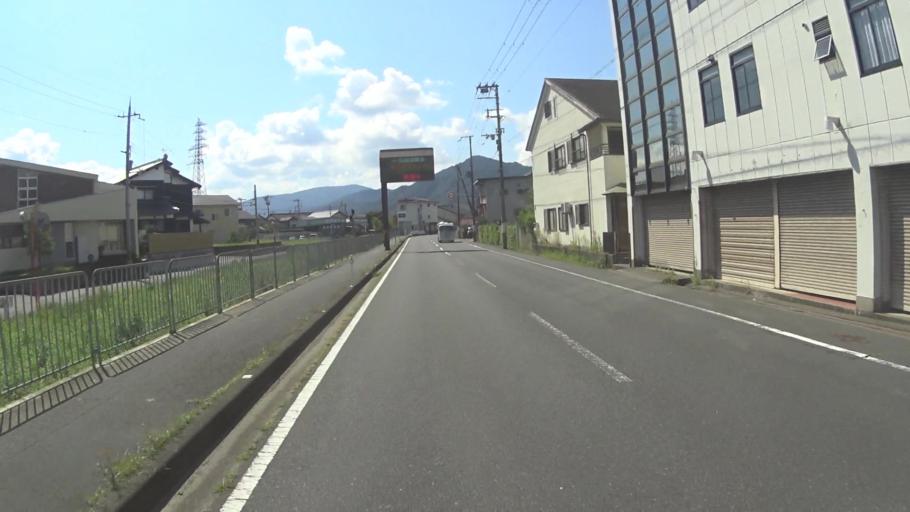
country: JP
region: Kyoto
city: Miyazu
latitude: 35.5376
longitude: 135.2045
